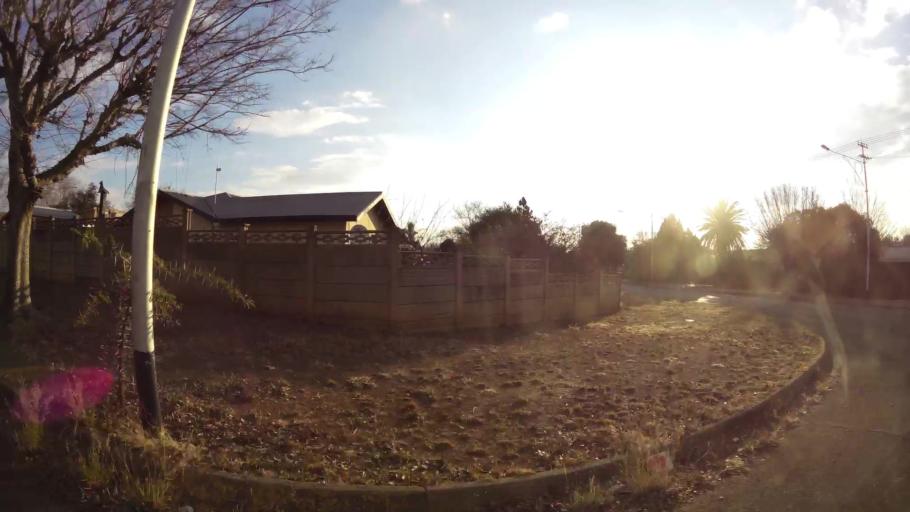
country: ZA
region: Orange Free State
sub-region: Mangaung Metropolitan Municipality
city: Bloemfontein
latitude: -29.1439
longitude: 26.1920
